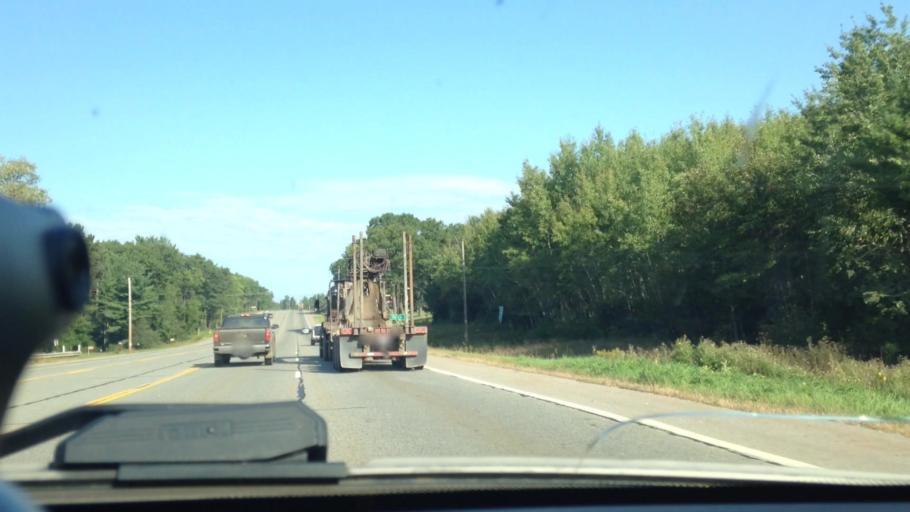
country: US
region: Michigan
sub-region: Dickinson County
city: Iron Mountain
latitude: 45.8529
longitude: -88.0547
